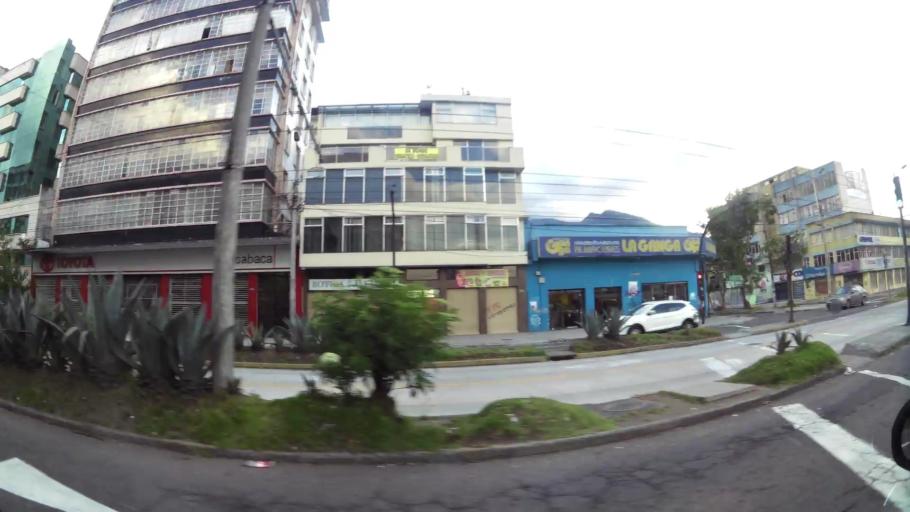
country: EC
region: Pichincha
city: Quito
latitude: -0.2024
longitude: -78.4978
